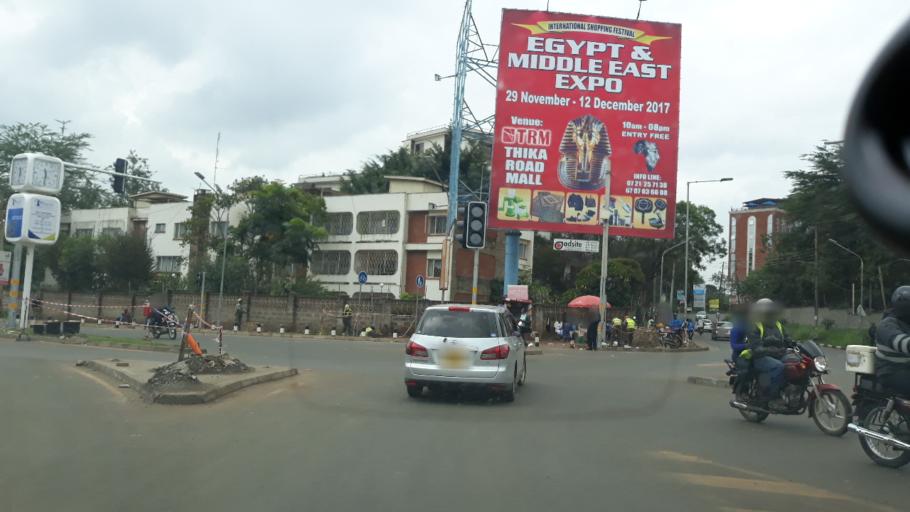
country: KE
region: Nairobi Area
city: Nairobi
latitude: -1.2658
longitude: 36.8009
